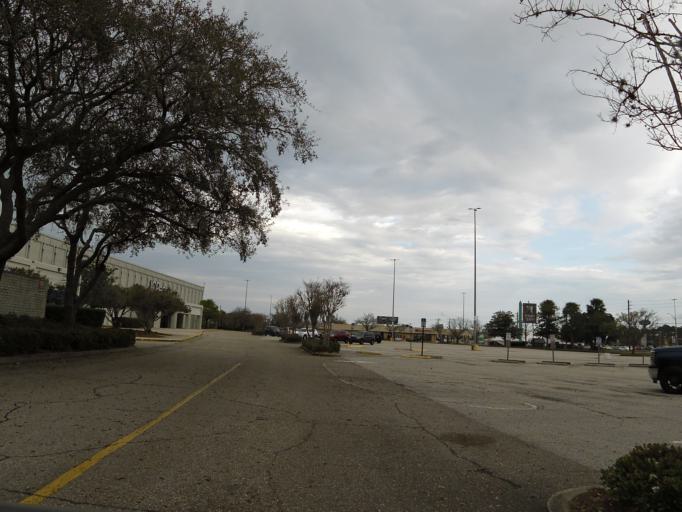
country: US
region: Florida
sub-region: Duval County
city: Jacksonville
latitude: 30.3227
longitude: -81.5497
